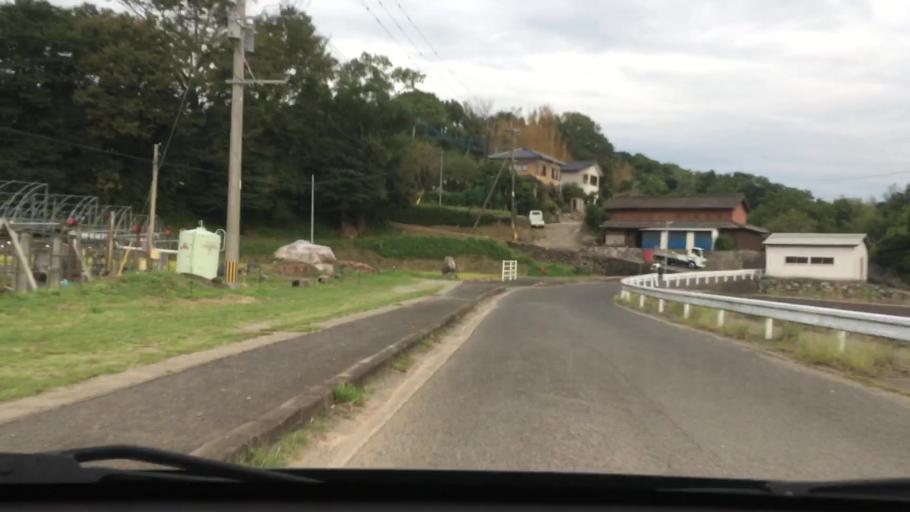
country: JP
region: Nagasaki
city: Sasebo
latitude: 33.0058
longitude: 129.7625
